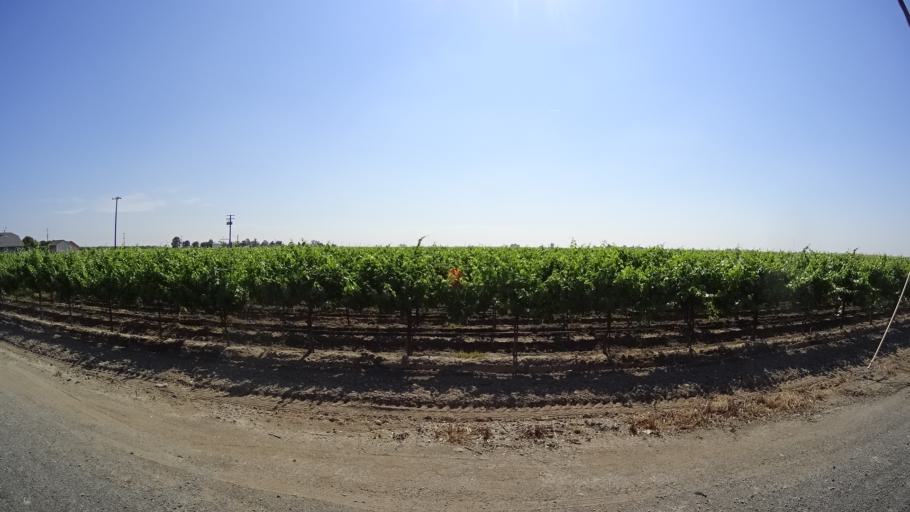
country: US
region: California
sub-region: Kings County
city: Hanford
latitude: 36.3400
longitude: -119.5830
